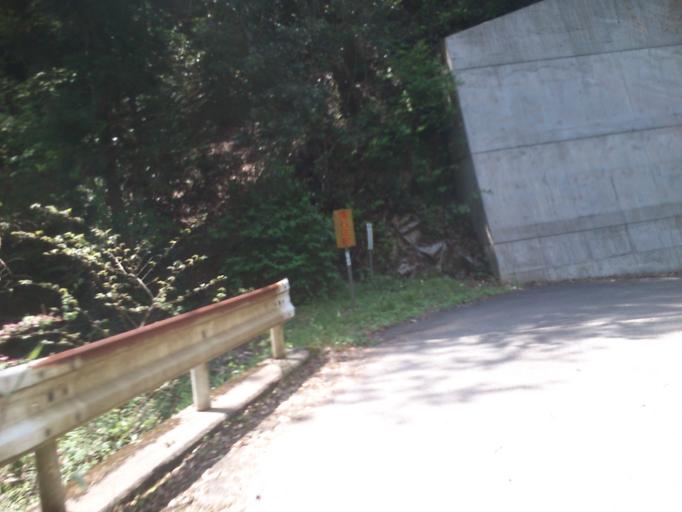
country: JP
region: Kyoto
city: Miyazu
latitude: 35.7020
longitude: 135.1203
